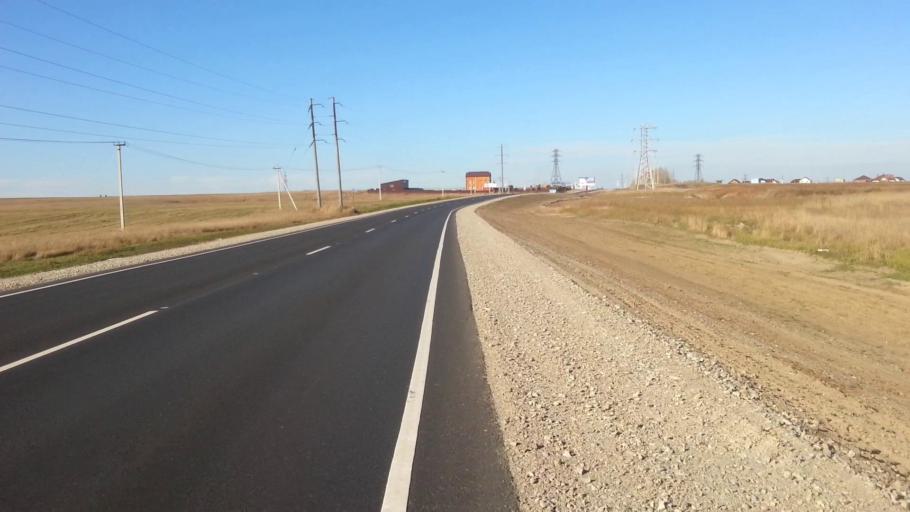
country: RU
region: Altai Krai
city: Sannikovo
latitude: 53.3320
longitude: 83.9362
